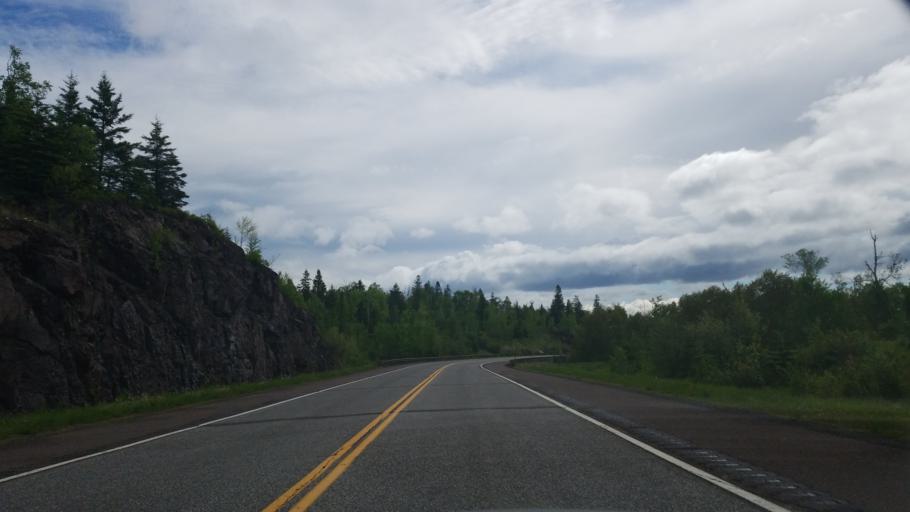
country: US
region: Minnesota
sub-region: Lake County
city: Two Harbors
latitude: 47.1454
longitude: -91.4624
